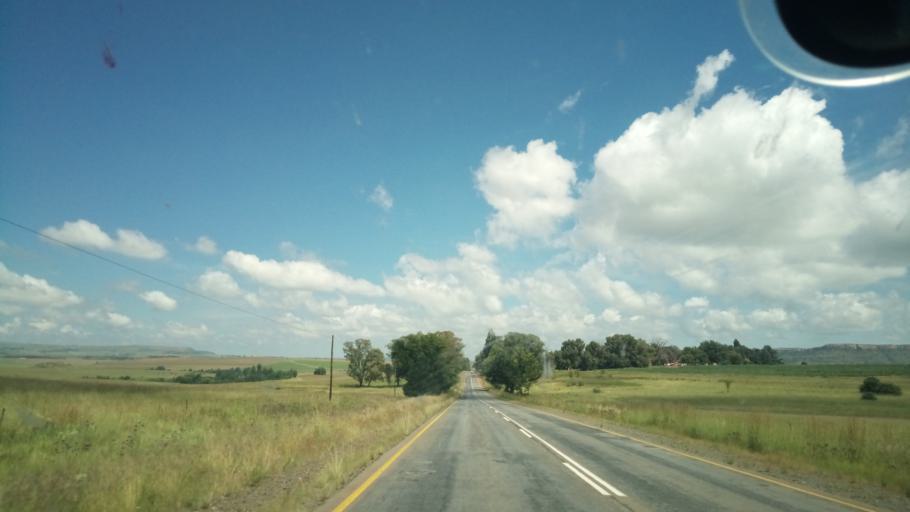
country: ZA
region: Orange Free State
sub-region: Thabo Mofutsanyana District Municipality
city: Ficksburg
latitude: -28.8973
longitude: 27.7772
